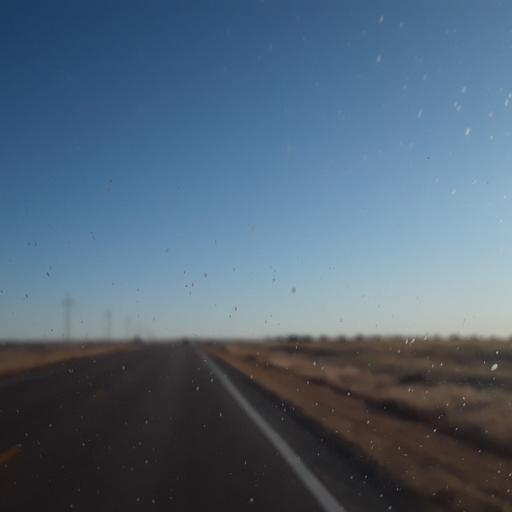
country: US
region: Kansas
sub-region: Wallace County
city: Sharon Springs
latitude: 38.9209
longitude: -101.7495
